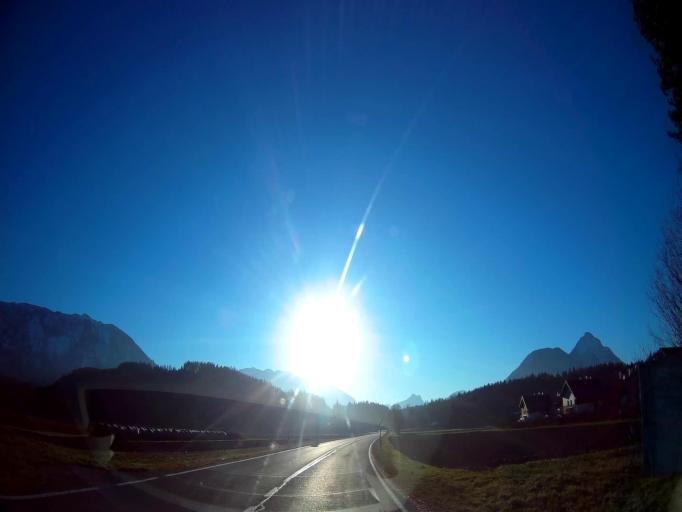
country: DE
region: Bavaria
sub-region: Upper Bavaria
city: Piding
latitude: 47.7721
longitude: 12.9585
